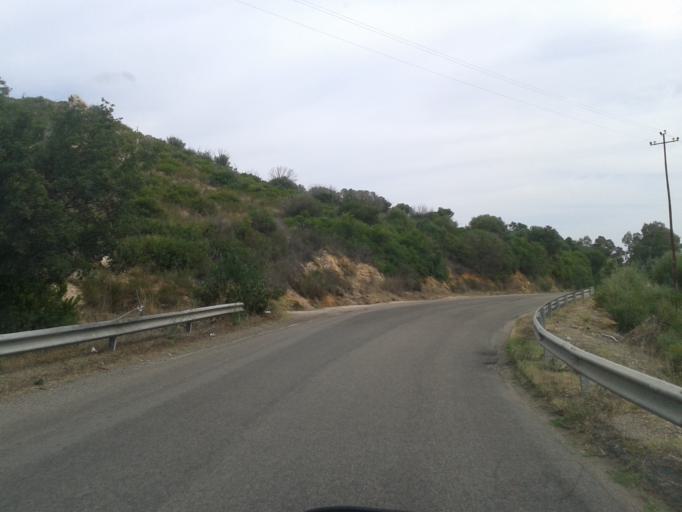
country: IT
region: Sardinia
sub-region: Provincia di Cagliari
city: Olia Speciosa
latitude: 39.2843
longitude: 9.5720
